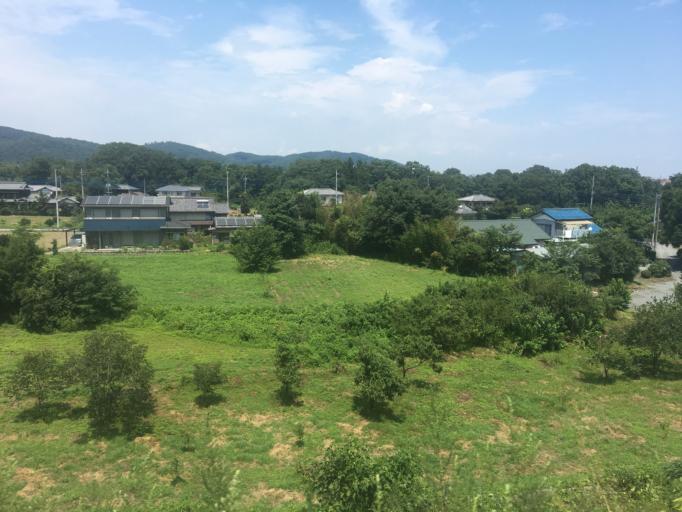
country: JP
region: Saitama
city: Yorii
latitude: 36.1082
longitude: 139.1872
